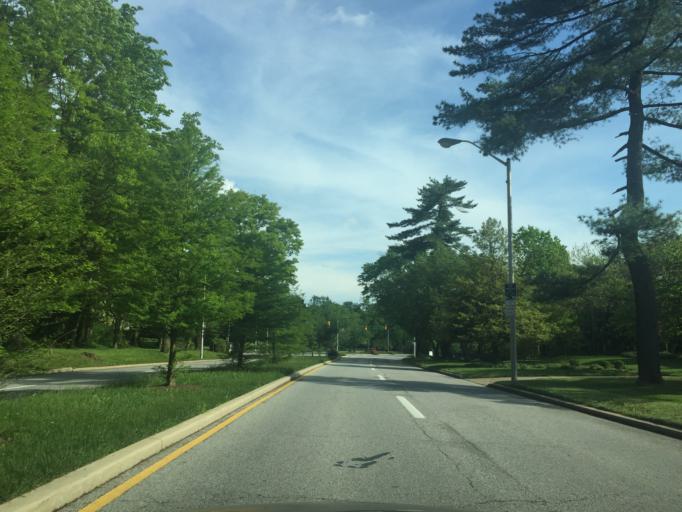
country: US
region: Maryland
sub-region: City of Baltimore
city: Baltimore
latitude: 39.3374
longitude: -76.6152
